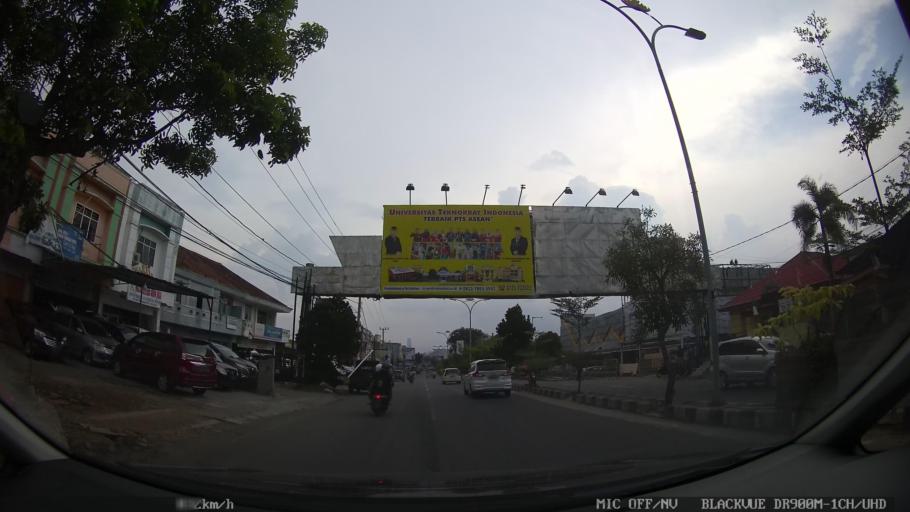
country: ID
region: Lampung
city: Kedaton
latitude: -5.4001
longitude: 105.2868
